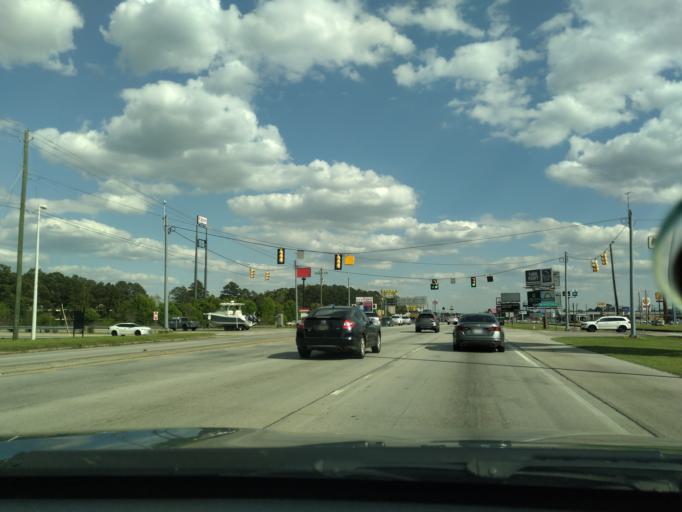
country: US
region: South Carolina
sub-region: Florence County
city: Florence
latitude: 34.2289
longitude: -79.7987
